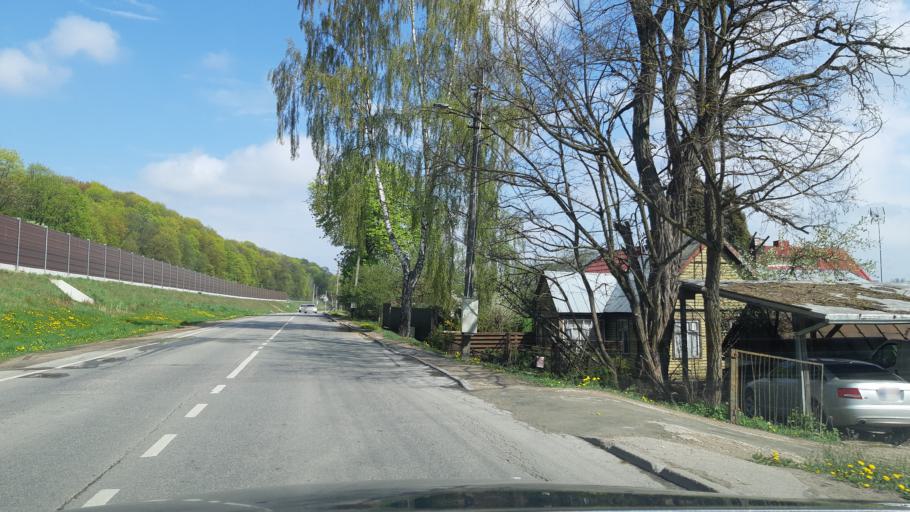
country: LT
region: Kauno apskritis
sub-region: Kaunas
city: Aleksotas
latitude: 54.8650
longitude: 23.9254
